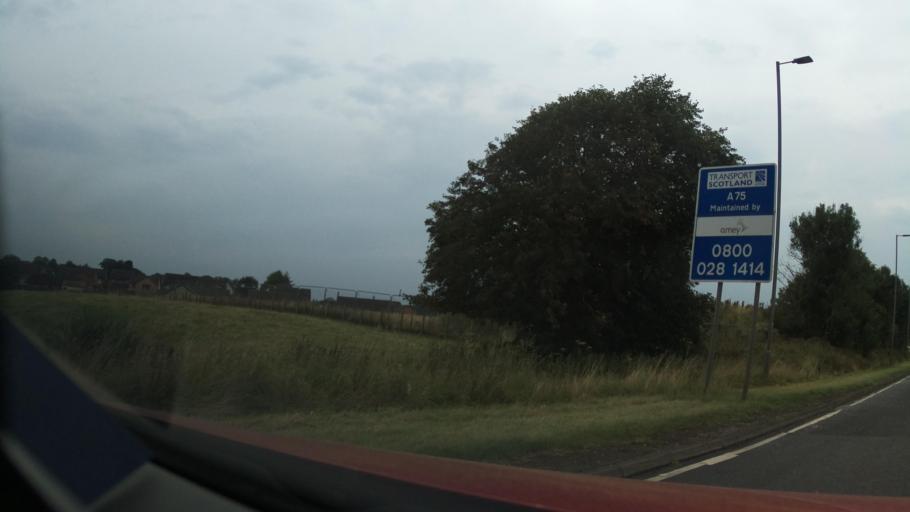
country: GB
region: Scotland
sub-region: Dumfries and Galloway
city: Gretna
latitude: 54.9999
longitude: -3.0717
